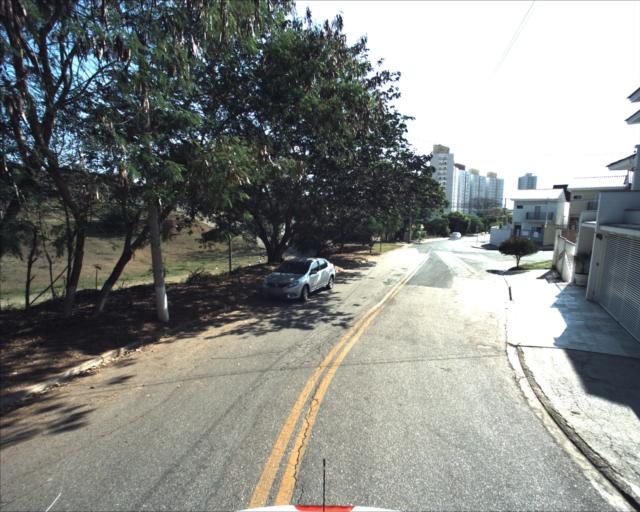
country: BR
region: Sao Paulo
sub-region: Sorocaba
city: Sorocaba
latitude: -23.4999
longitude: -47.4261
